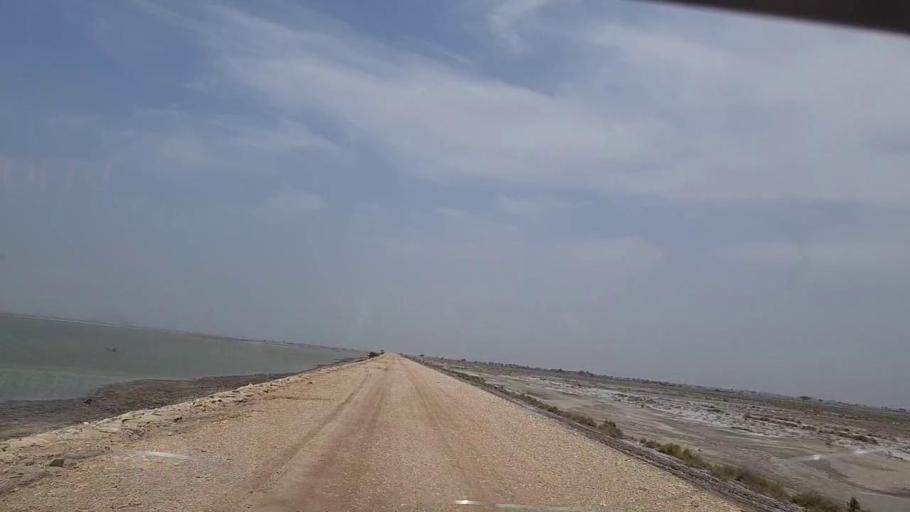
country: PK
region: Sindh
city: Sehwan
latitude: 26.4143
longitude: 67.7683
